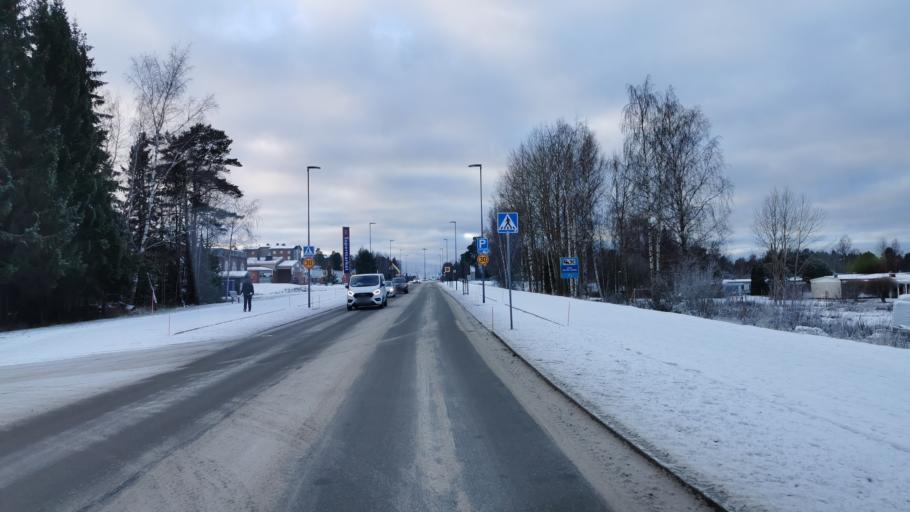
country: FI
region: Ostrobothnia
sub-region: Vaasa
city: Korsholm
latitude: 63.1140
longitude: 21.6817
